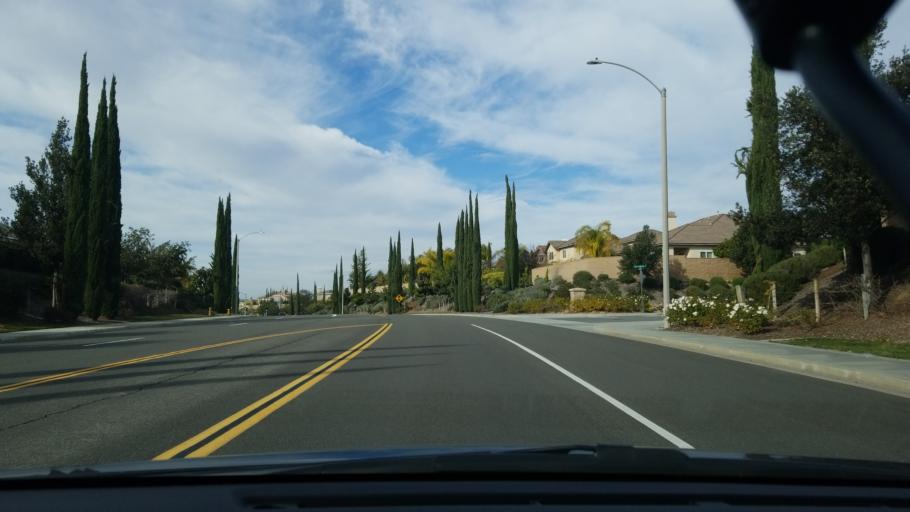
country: US
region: California
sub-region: Riverside County
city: Temecula
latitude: 33.4742
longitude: -117.0642
